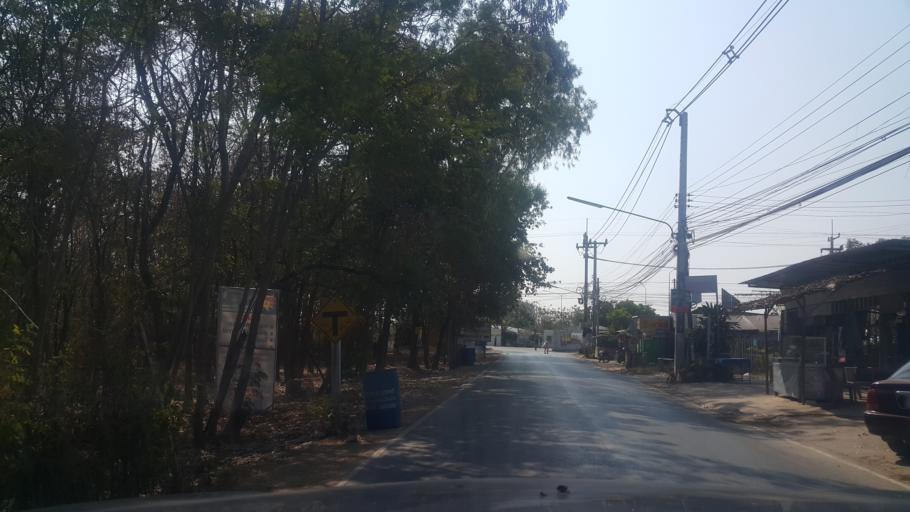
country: TH
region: Nakhon Ratchasima
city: Nakhon Ratchasima
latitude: 14.9317
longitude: 102.0439
